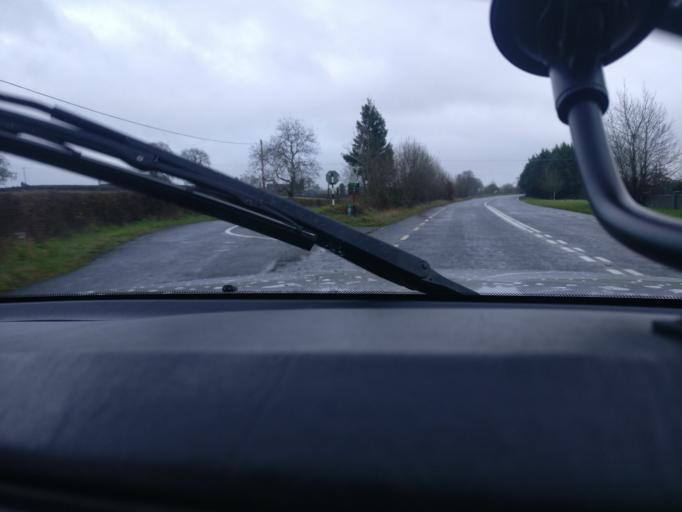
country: IE
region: Leinster
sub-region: An Mhi
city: Longwood
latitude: 53.4301
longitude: -6.9241
